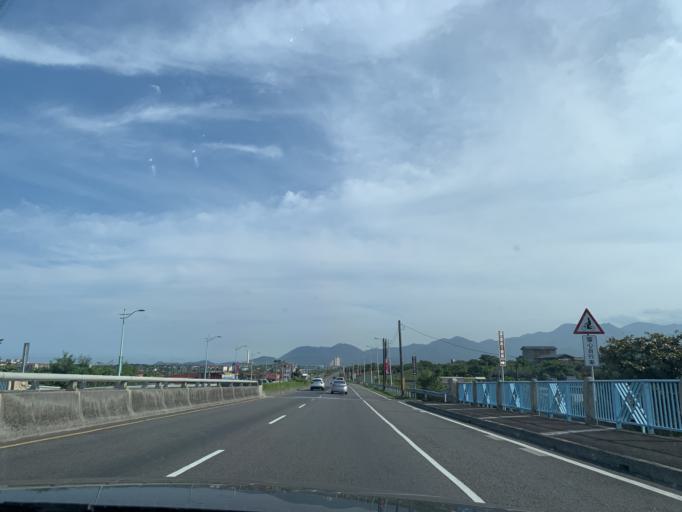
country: TW
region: Taiwan
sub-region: Yilan
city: Yilan
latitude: 24.6915
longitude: 121.8248
